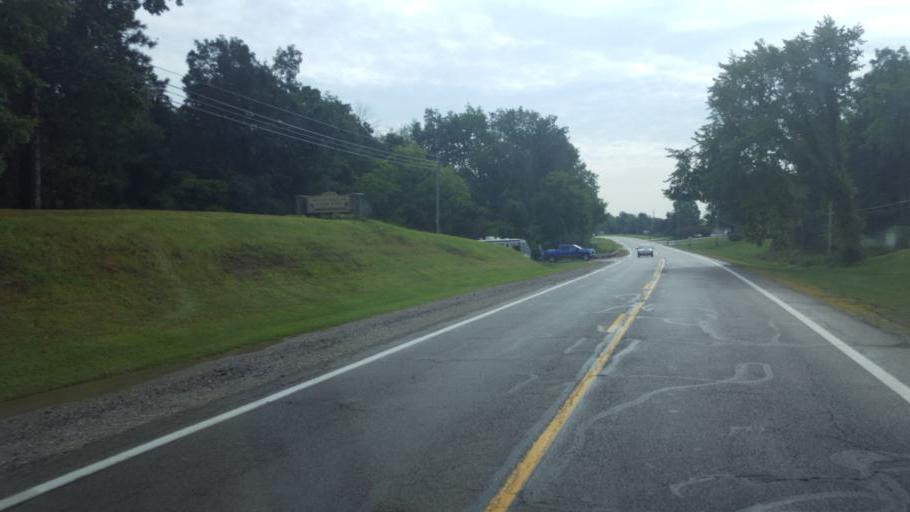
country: US
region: Ohio
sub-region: Morrow County
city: Mount Gilead
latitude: 40.5459
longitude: -82.8098
